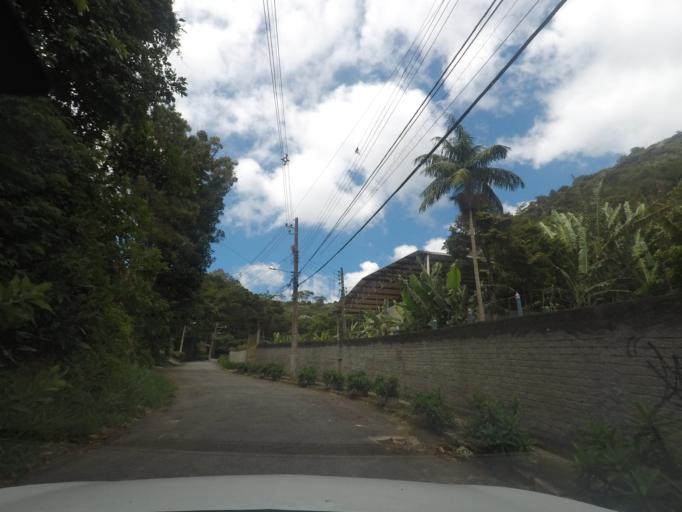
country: BR
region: Rio de Janeiro
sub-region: Teresopolis
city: Teresopolis
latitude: -22.4037
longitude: -42.9805
